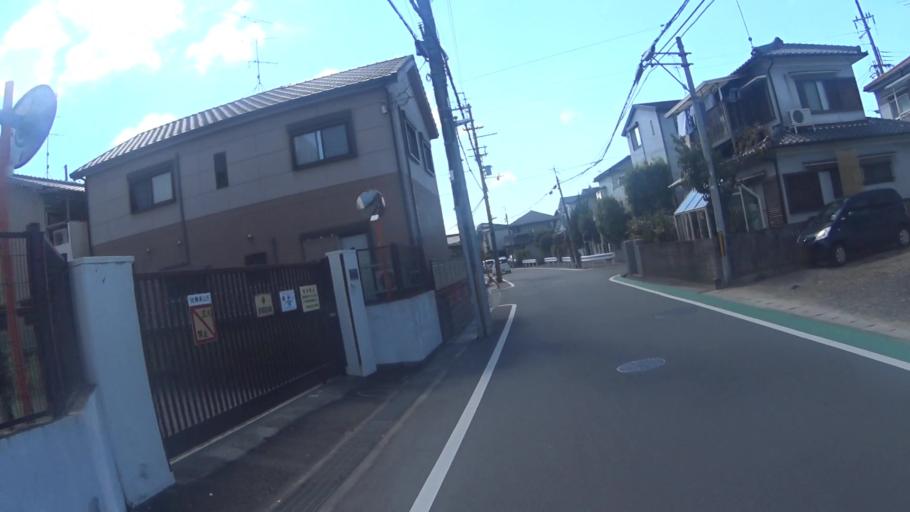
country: JP
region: Kyoto
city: Tanabe
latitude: 34.8291
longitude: 135.8033
